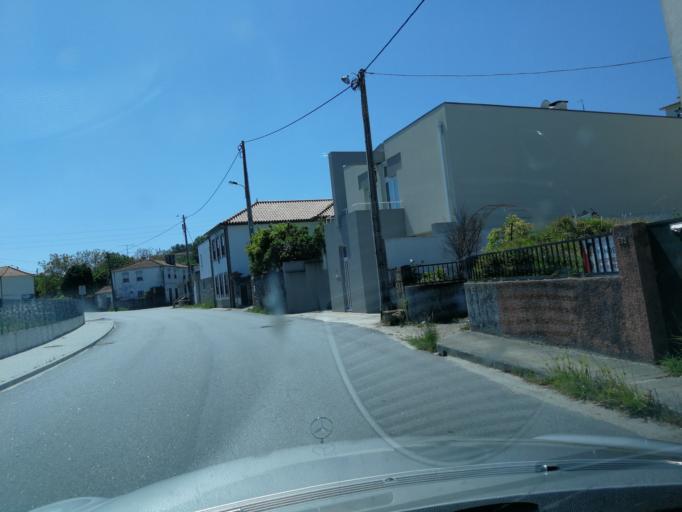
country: PT
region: Viana do Castelo
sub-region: Viana do Castelo
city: Meadela
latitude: 41.7121
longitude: -8.8026
